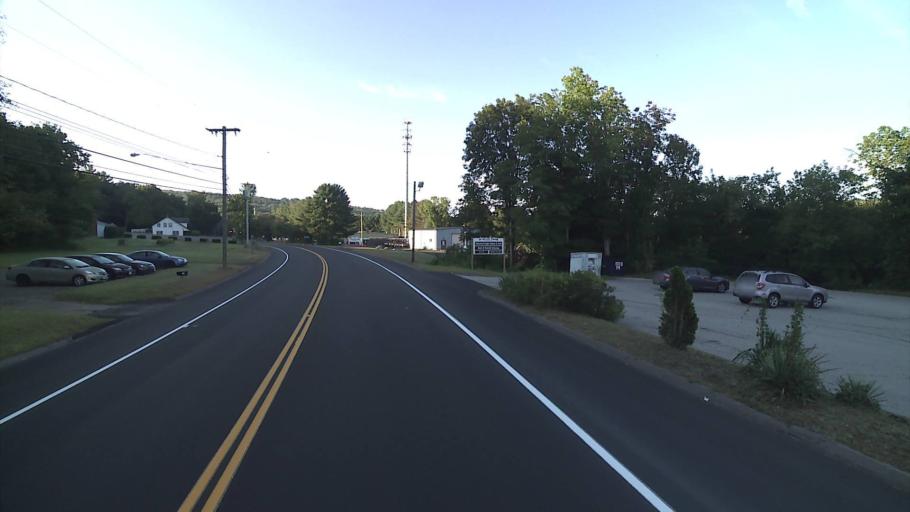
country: US
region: Connecticut
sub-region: Tolland County
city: Storrs
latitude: 41.8377
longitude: -72.3077
